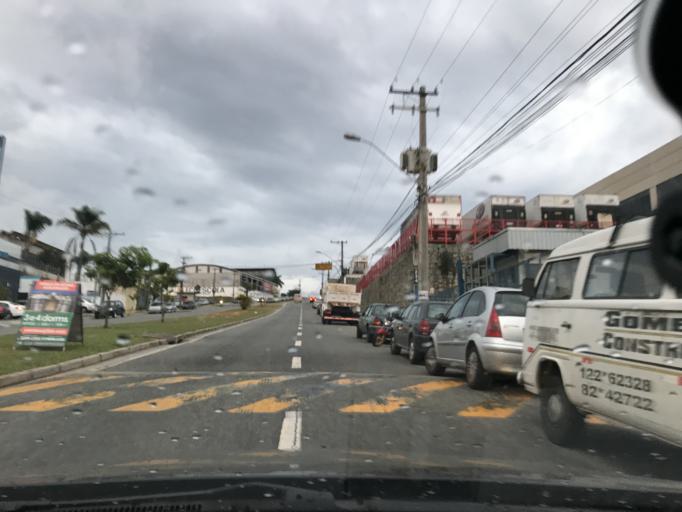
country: BR
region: Sao Paulo
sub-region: Carapicuiba
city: Carapicuiba
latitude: -23.4928
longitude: -46.8306
